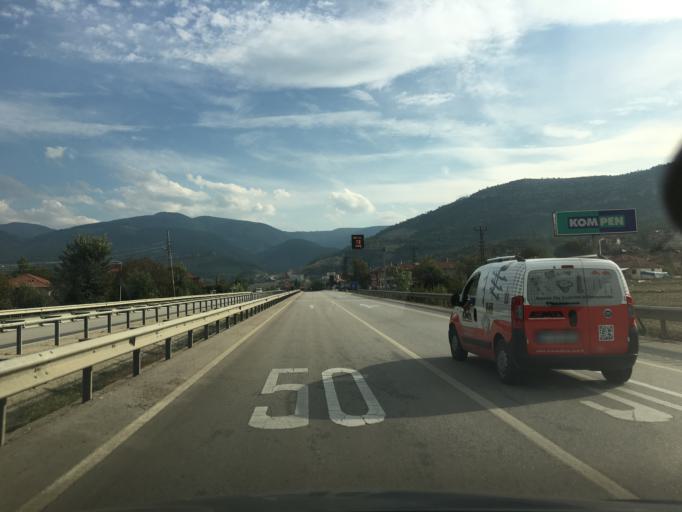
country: TR
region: Karabuk
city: Karabuk
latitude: 41.1063
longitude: 32.6688
